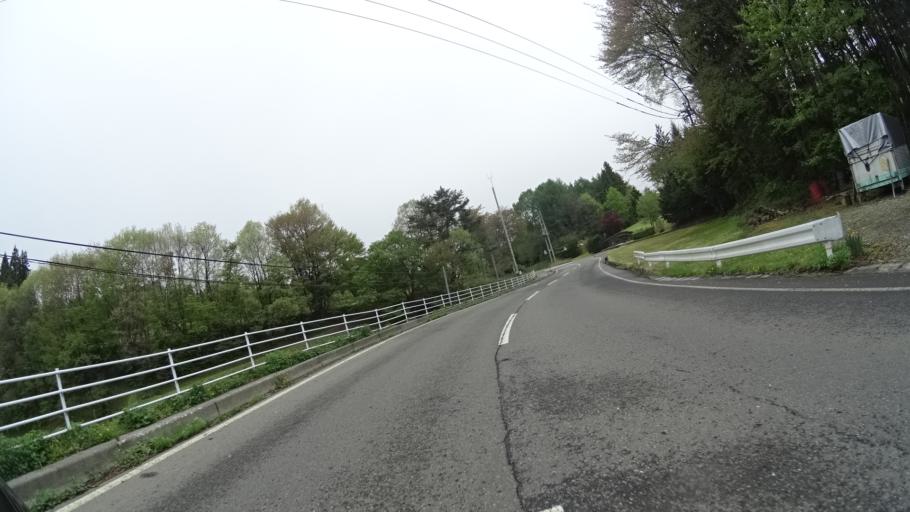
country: JP
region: Nagano
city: Nagano-shi
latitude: 36.7613
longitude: 138.1980
